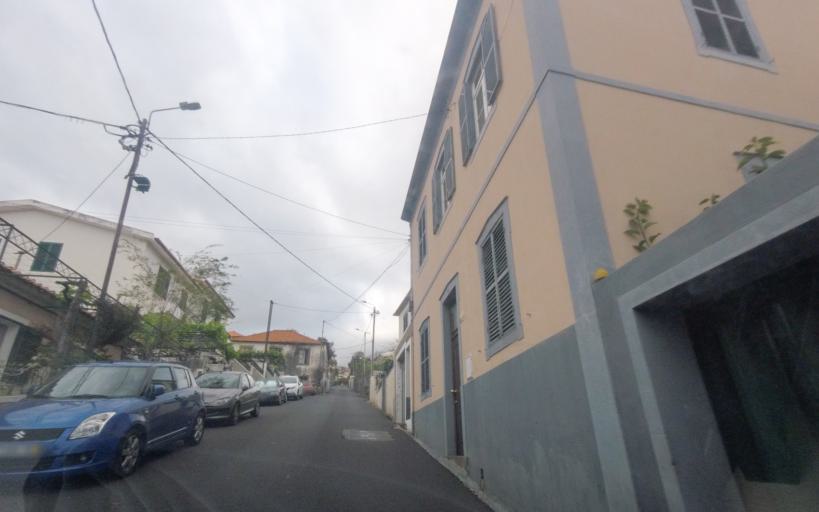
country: PT
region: Madeira
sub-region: Funchal
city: Nossa Senhora do Monte
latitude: 32.6532
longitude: -16.8978
